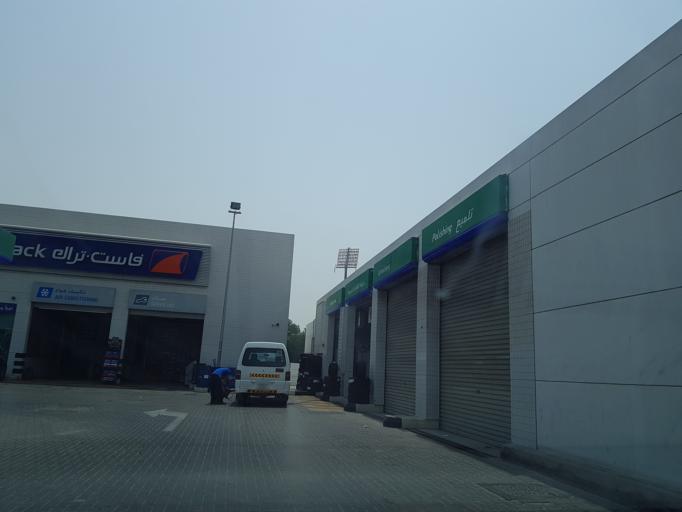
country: AE
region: Ash Shariqah
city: Sharjah
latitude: 25.2248
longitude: 55.3229
